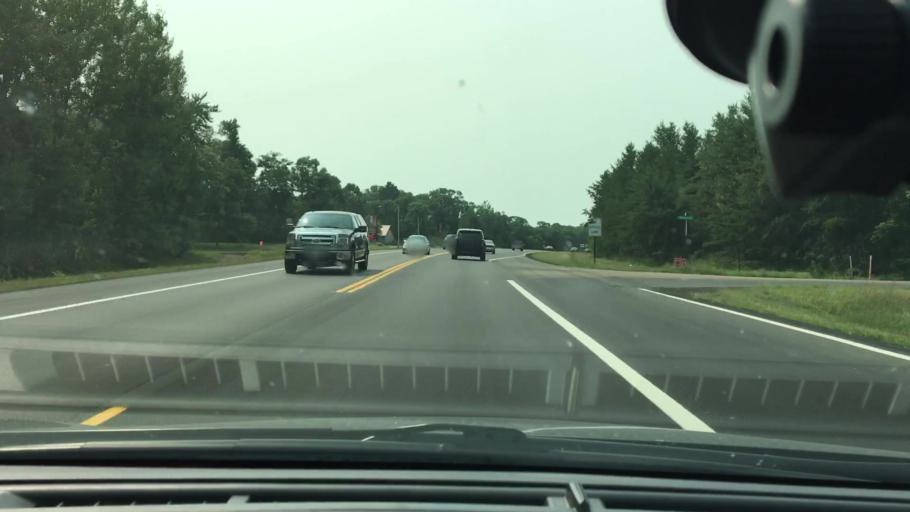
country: US
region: Minnesota
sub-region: Crow Wing County
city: Brainerd
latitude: 46.4383
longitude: -94.1715
